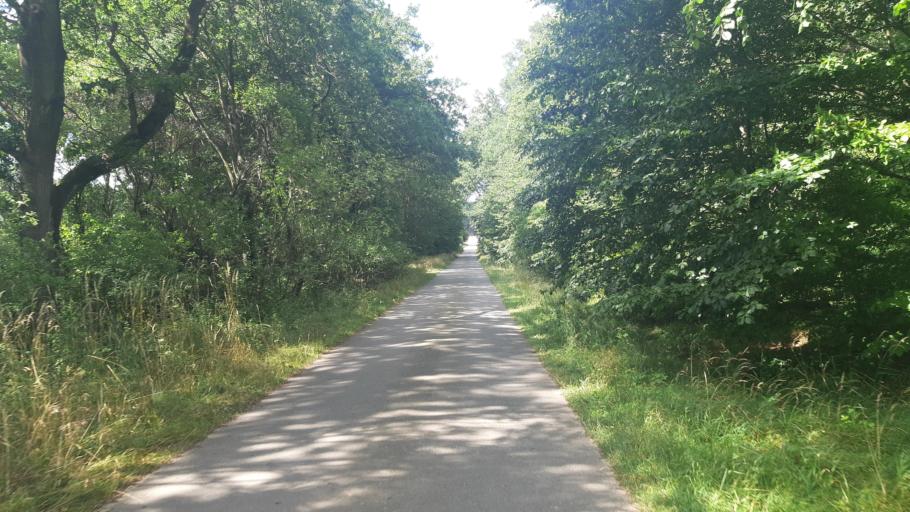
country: DE
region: Lower Saxony
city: Tosterglope
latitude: 53.2020
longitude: 10.7951
